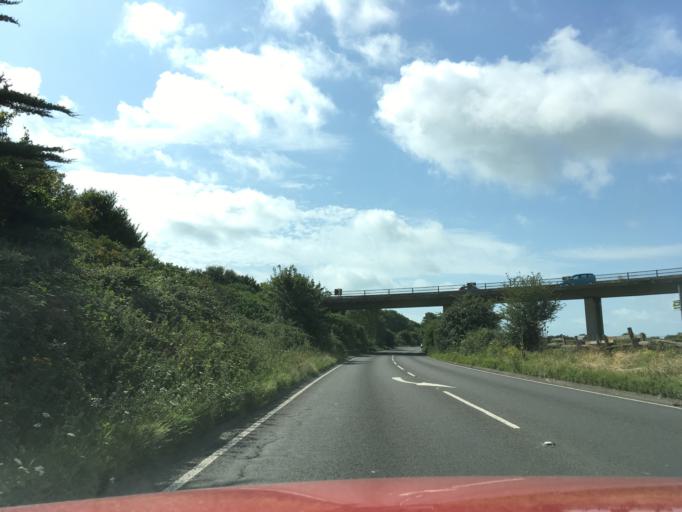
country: GB
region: England
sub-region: West Sussex
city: Shoreham-by-Sea
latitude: 50.8441
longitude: -0.2850
